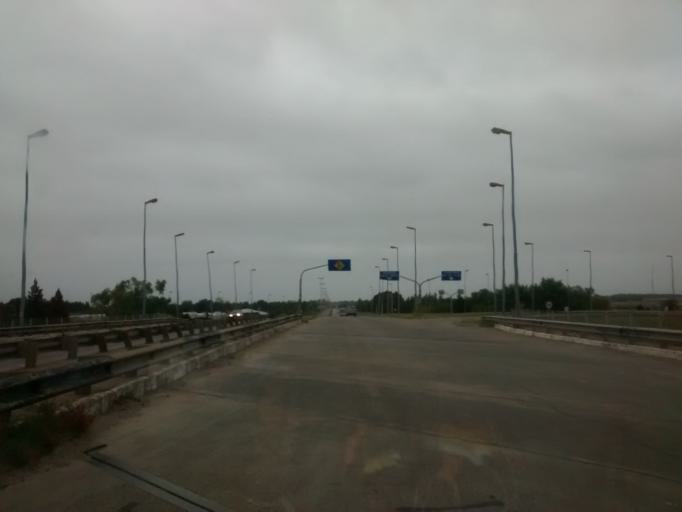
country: AR
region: Buenos Aires
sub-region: Partido de La Plata
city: La Plata
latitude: -35.0355
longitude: -58.0926
